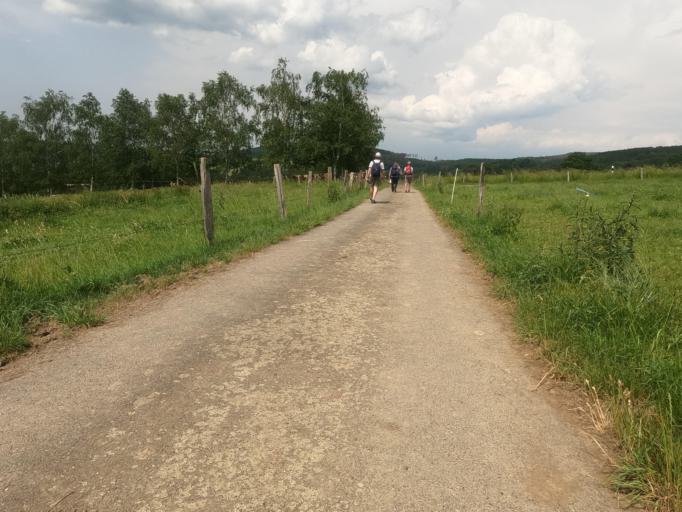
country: DE
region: Rheinland-Pfalz
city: Unnau
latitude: 50.6434
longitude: 7.9064
